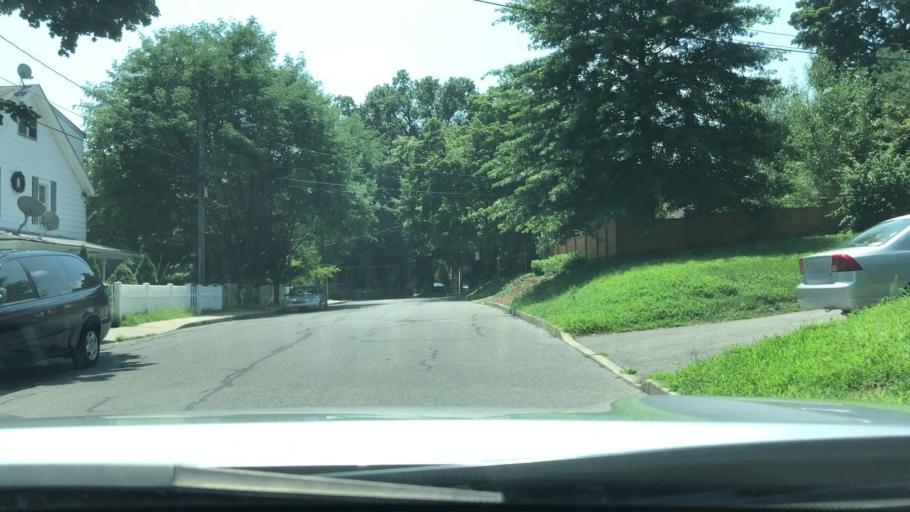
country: US
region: New York
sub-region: Dutchess County
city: Beacon
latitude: 41.5010
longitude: -73.9723
